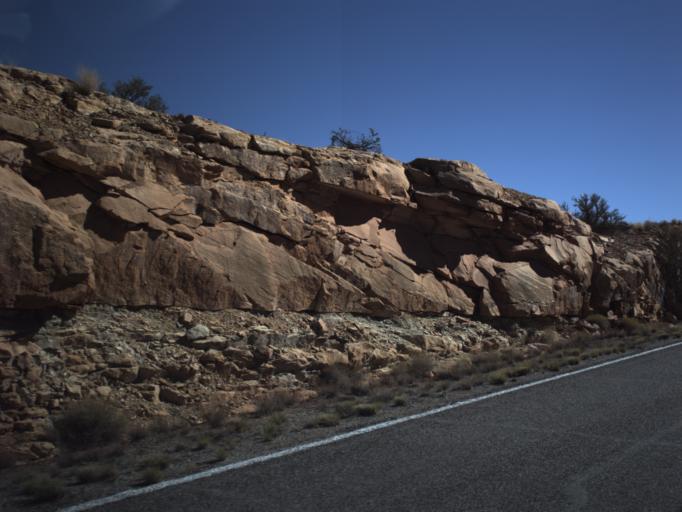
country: US
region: Utah
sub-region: San Juan County
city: Blanding
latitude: 37.8817
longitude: -110.3574
